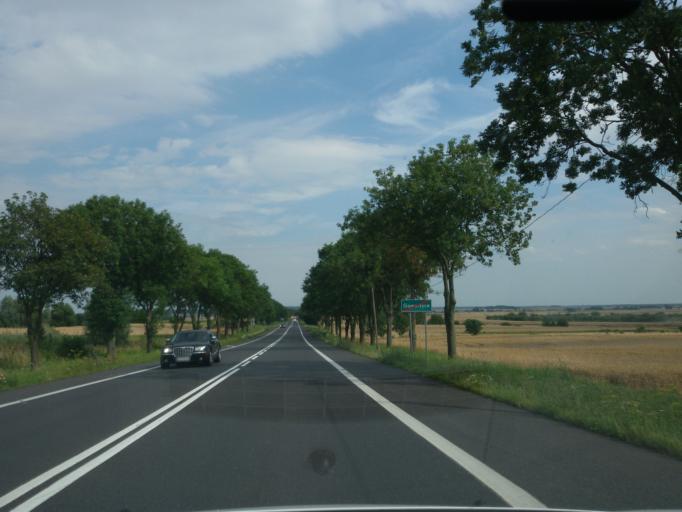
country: PL
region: Lower Silesian Voivodeship
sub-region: Powiat polkowicki
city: Gaworzyce
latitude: 51.6344
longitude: 15.8961
